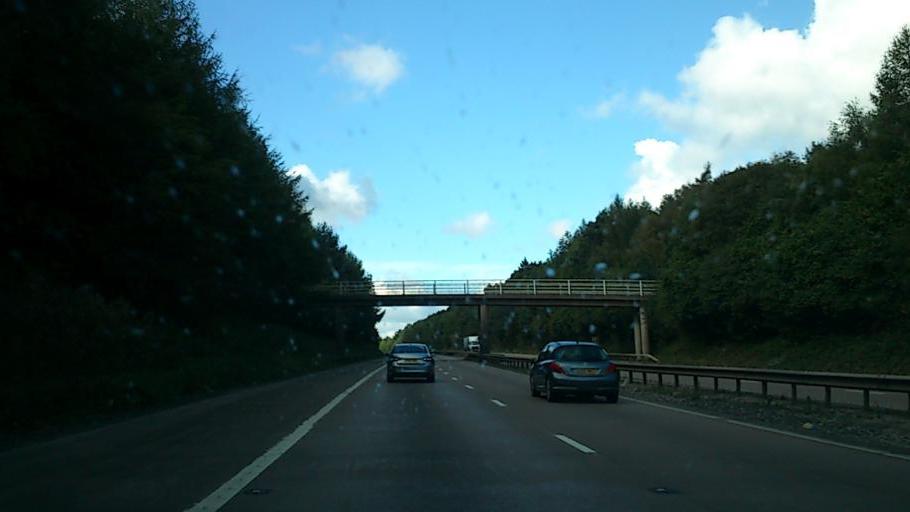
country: GB
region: England
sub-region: Staffordshire
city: Codsall
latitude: 52.6462
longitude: -2.2243
